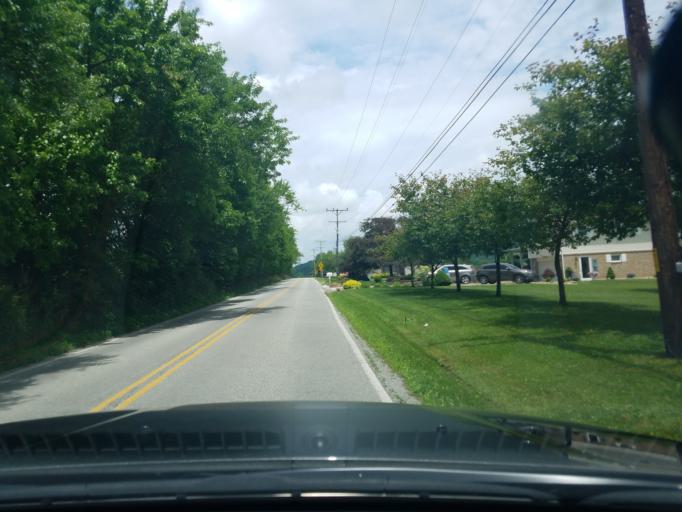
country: US
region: Pennsylvania
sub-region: Westmoreland County
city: Youngwood
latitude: 40.2148
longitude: -79.5390
